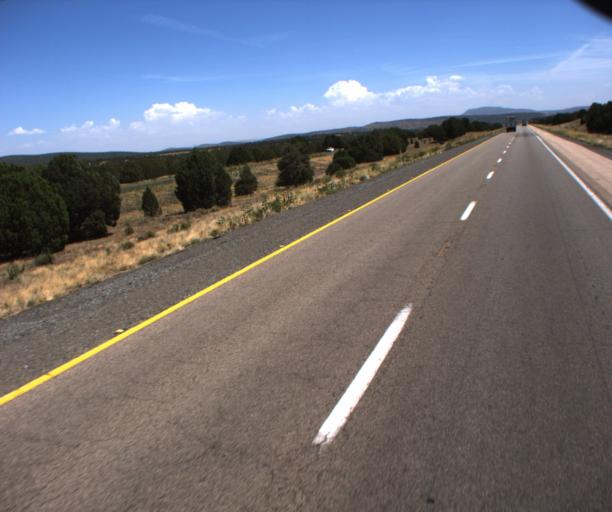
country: US
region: Arizona
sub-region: Mohave County
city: Peach Springs
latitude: 35.2114
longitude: -113.2623
